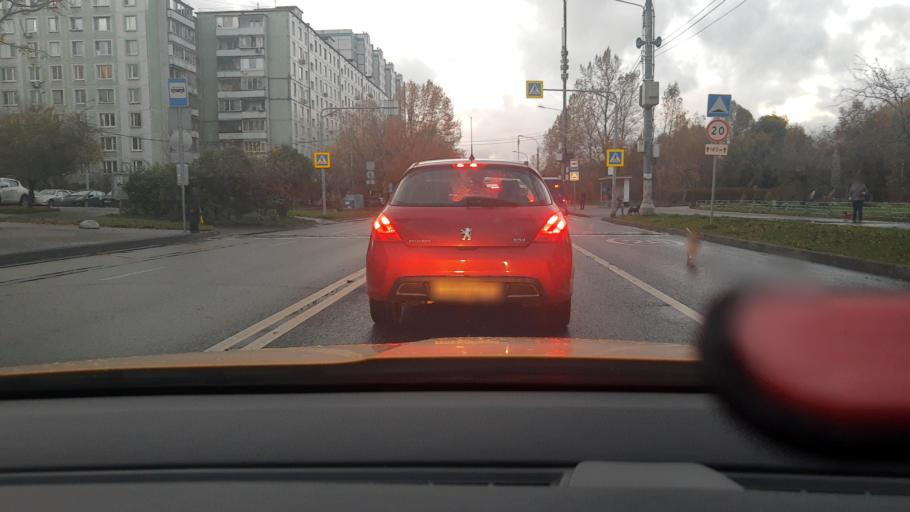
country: RU
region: Moscow
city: Strogino
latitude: 55.8126
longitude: 37.4107
